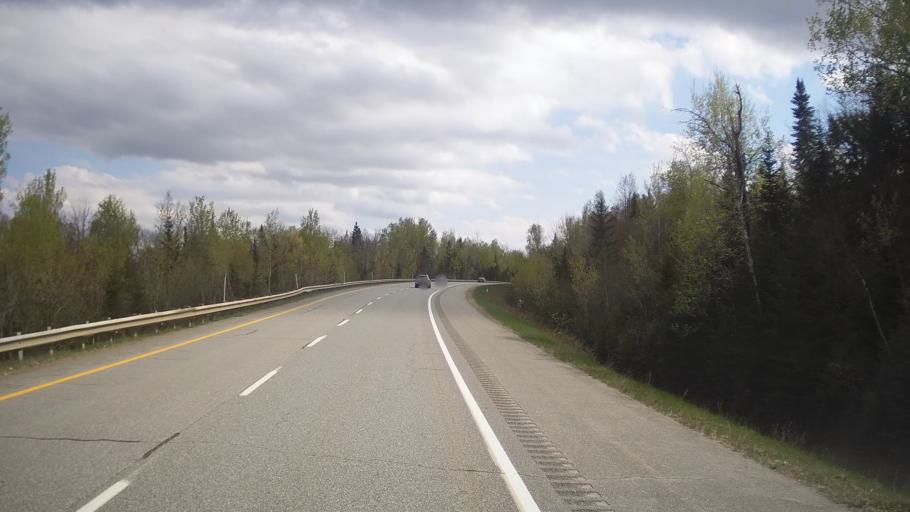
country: CA
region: Quebec
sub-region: Estrie
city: Magog
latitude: 45.1546
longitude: -72.0663
